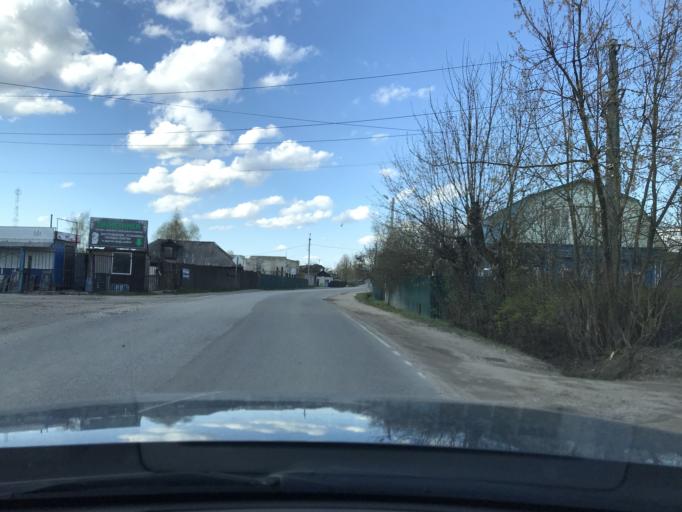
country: RU
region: Vladimir
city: Strunino
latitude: 56.3811
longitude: 38.5783
